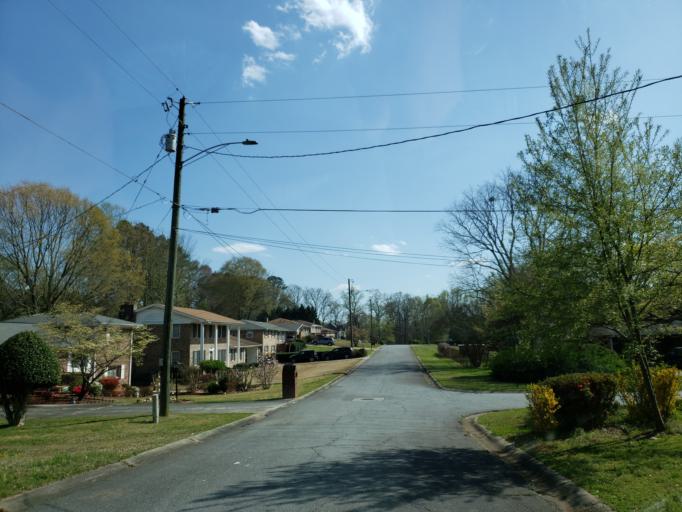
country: US
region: Georgia
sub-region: Cobb County
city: Kennesaw
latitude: 34.0316
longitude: -84.5470
